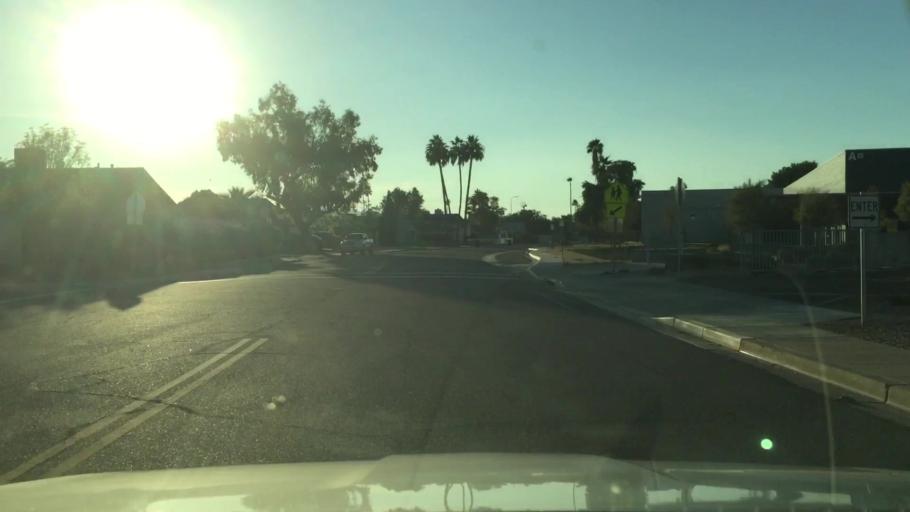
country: US
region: Arizona
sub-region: Maricopa County
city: Tempe
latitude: 33.3837
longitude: -111.9154
